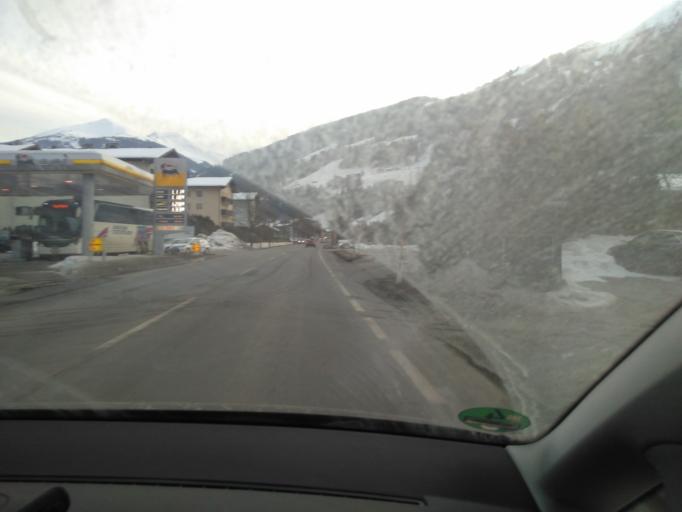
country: AT
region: Salzburg
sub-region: Politischer Bezirk Sankt Johann im Pongau
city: Bad Hofgastein
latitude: 47.1773
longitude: 13.1009
